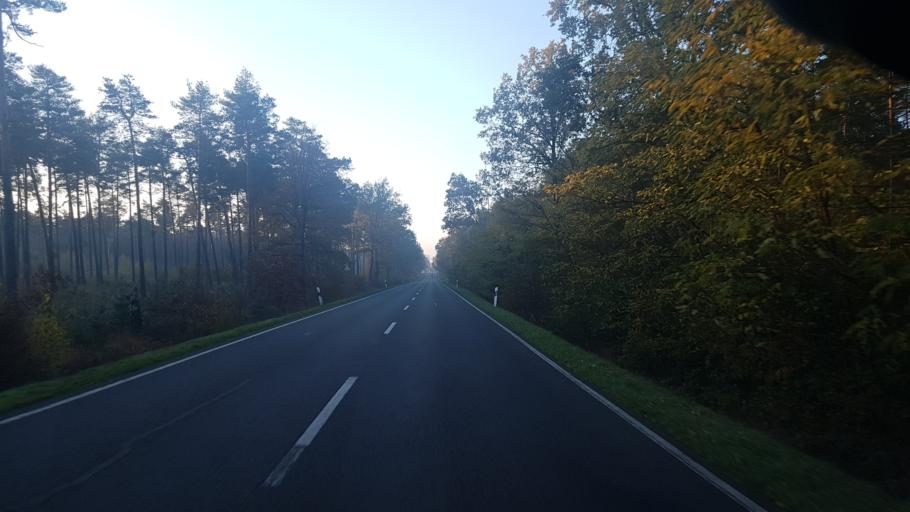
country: DE
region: Saxony
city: Schildau
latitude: 51.4734
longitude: 12.9799
